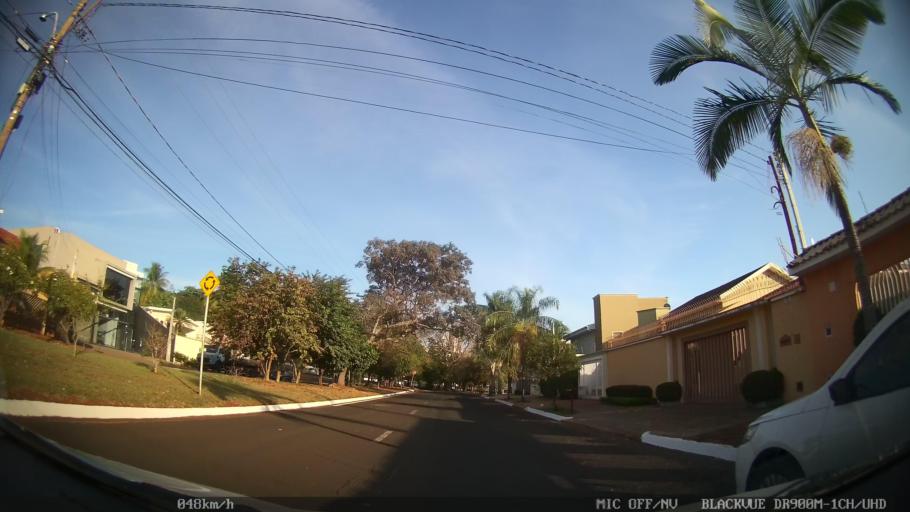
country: BR
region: Sao Paulo
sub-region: Ribeirao Preto
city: Ribeirao Preto
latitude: -21.2111
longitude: -47.7872
